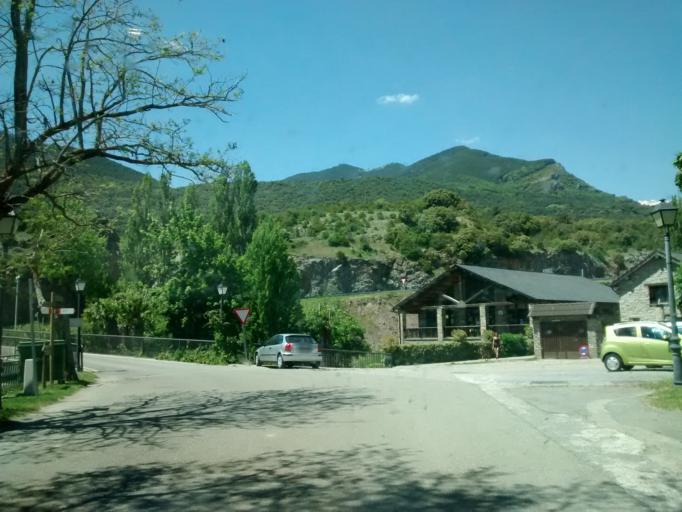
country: ES
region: Aragon
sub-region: Provincia de Huesca
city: Villanua
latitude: 42.6823
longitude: -0.5321
